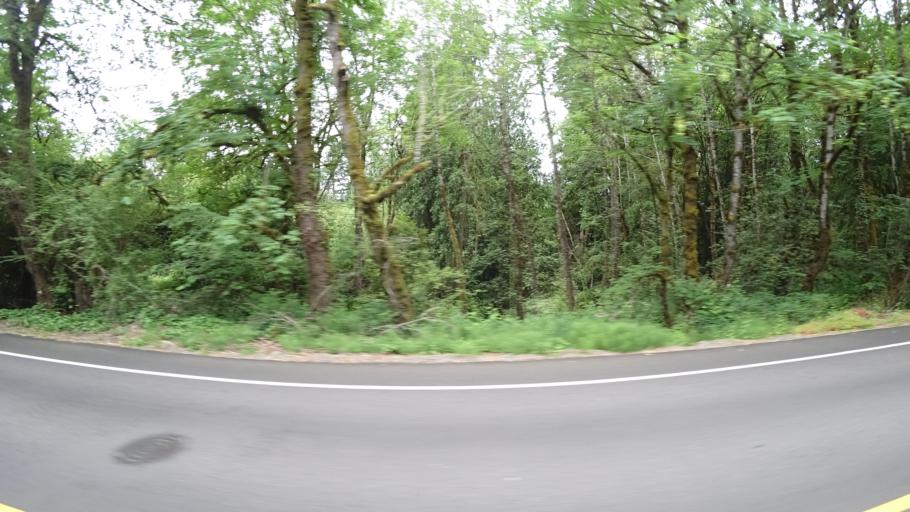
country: US
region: Oregon
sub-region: Clackamas County
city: Lake Oswego
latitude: 45.4395
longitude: -122.6692
